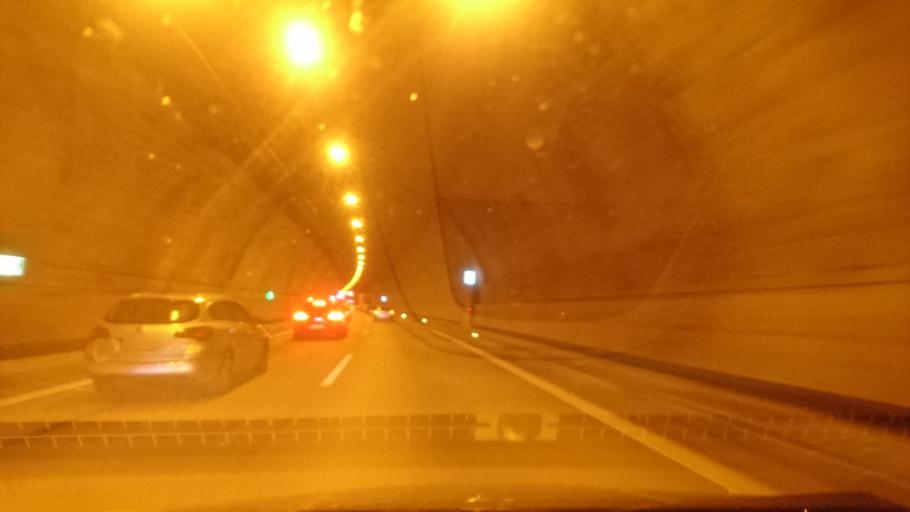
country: DE
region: Bavaria
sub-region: Upper Palatinate
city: Lappersdorf
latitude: 49.0316
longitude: 12.0825
